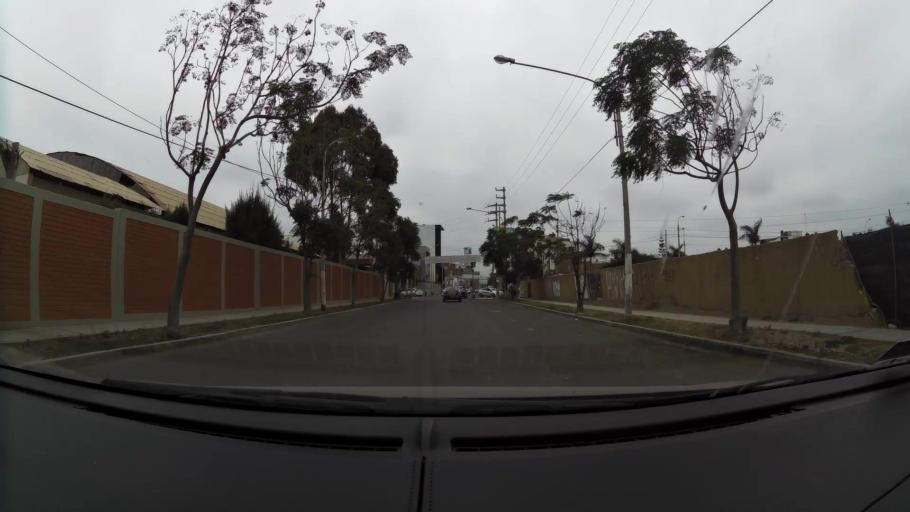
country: PE
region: La Libertad
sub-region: Provincia de Trujillo
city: Buenos Aires
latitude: -8.1339
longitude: -79.0385
